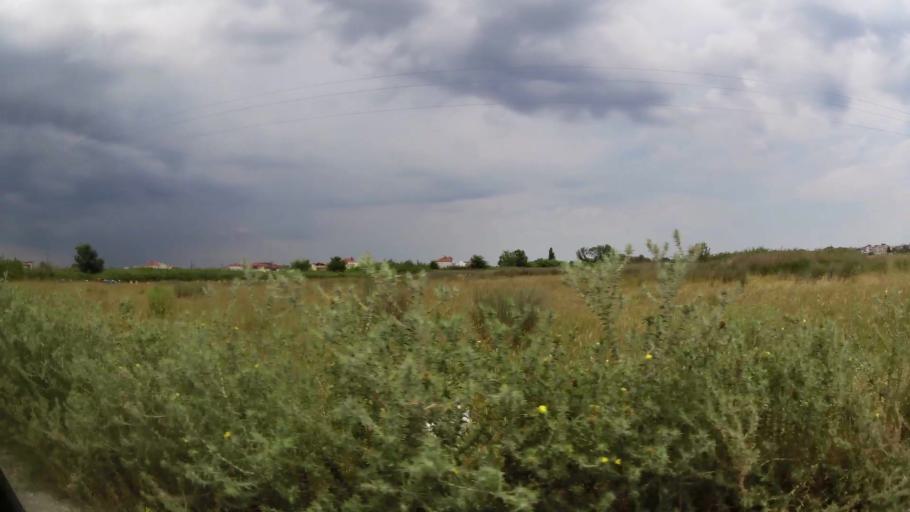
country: GR
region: Central Macedonia
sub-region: Nomos Pierias
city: Paralia
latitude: 40.2746
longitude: 22.5890
